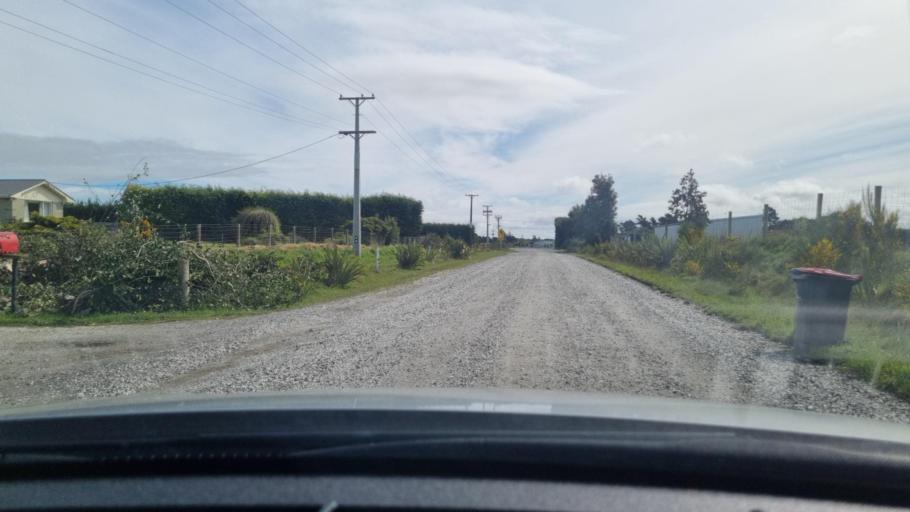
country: NZ
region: Southland
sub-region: Invercargill City
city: Invercargill
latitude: -46.4507
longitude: 168.3832
